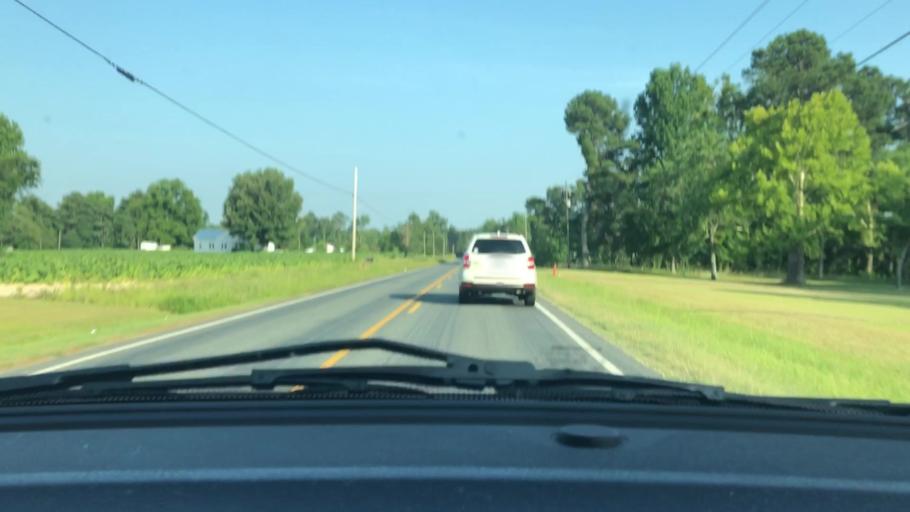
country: US
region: North Carolina
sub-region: Lee County
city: Broadway
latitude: 35.3511
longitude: -79.0732
